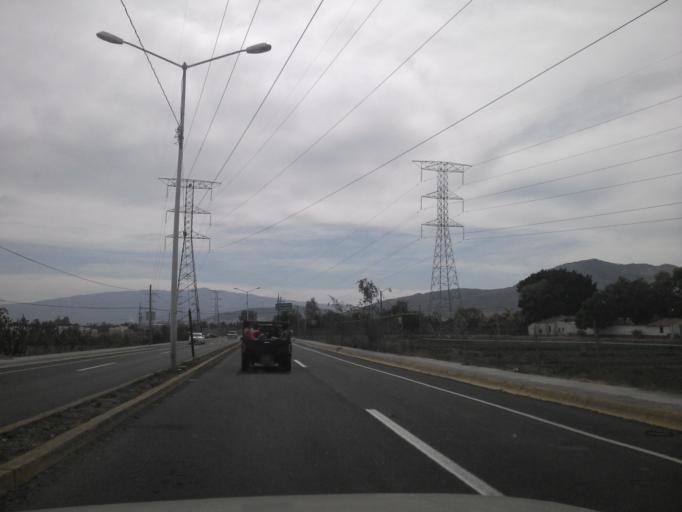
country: MX
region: Jalisco
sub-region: Tlajomulco de Zuniga
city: Hacienda los Fresnos
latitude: 20.5321
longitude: -103.4061
